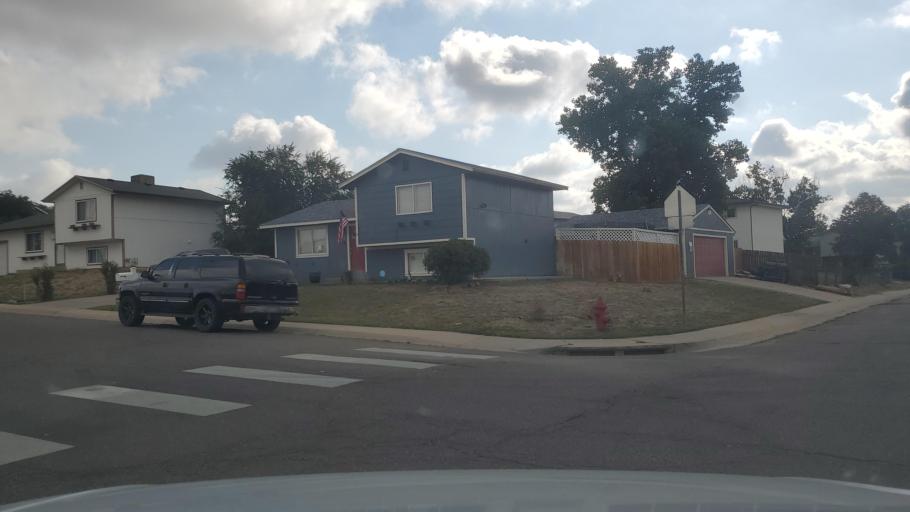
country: US
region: Colorado
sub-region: Adams County
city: Welby
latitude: 39.8464
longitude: -104.9687
